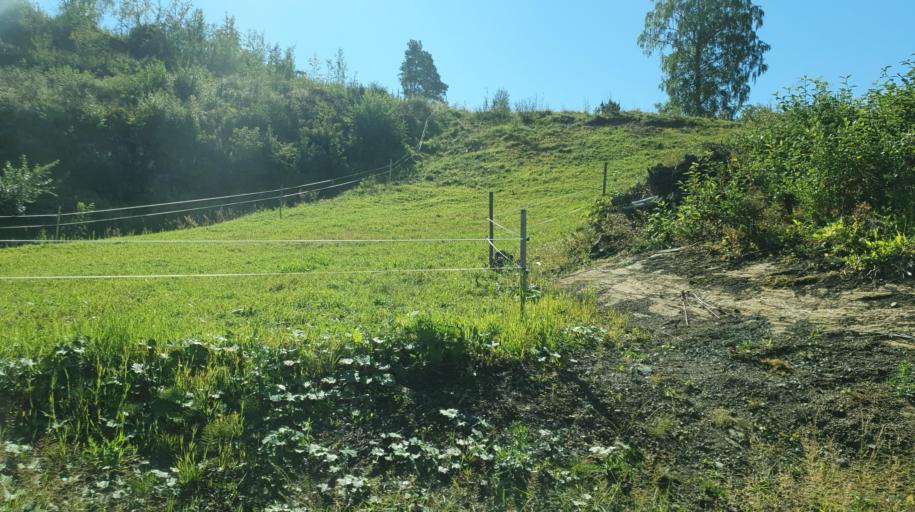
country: NO
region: Nord-Trondelag
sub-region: Verdal
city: Verdal
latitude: 63.7733
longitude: 11.4062
